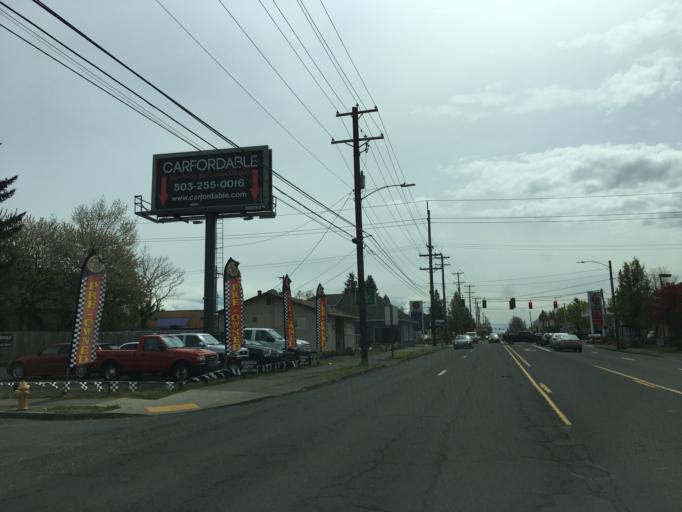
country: US
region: Oregon
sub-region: Multnomah County
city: Lents
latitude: 45.5489
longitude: -122.5787
